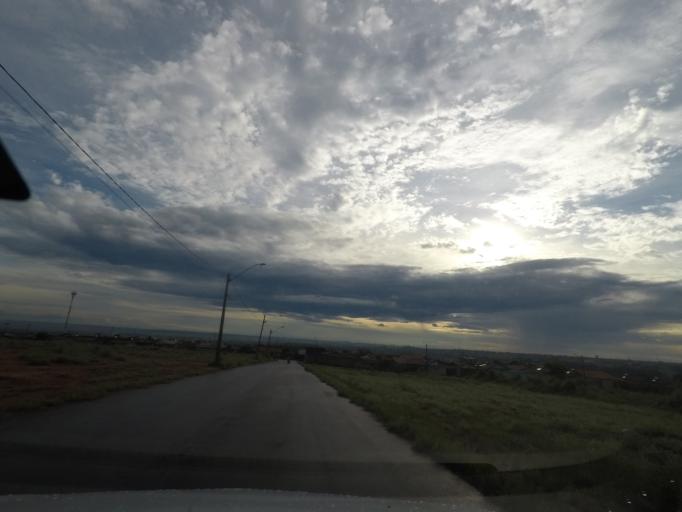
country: BR
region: Goias
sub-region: Goiania
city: Goiania
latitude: -16.7552
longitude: -49.3782
